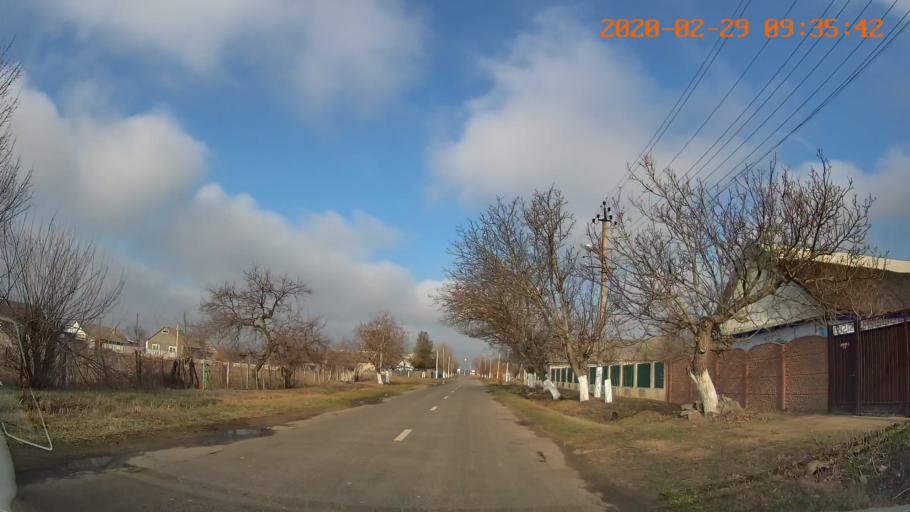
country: MD
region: Telenesti
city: Dnestrovsc
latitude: 46.6205
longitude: 29.8966
